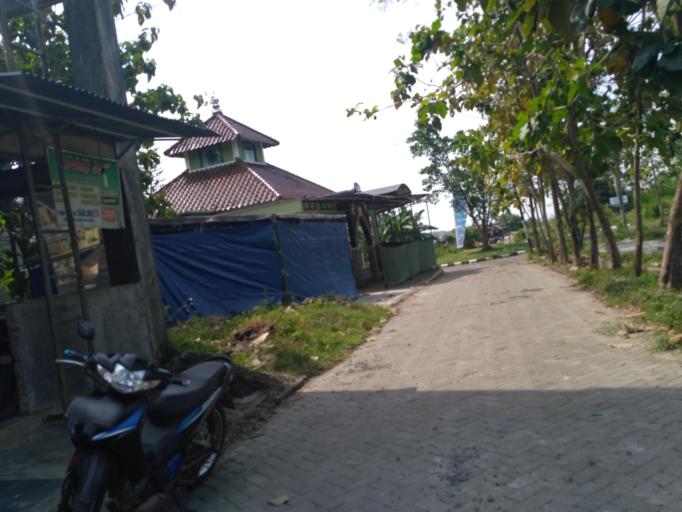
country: ID
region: Central Java
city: Semarang
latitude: -7.0437
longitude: 110.4425
